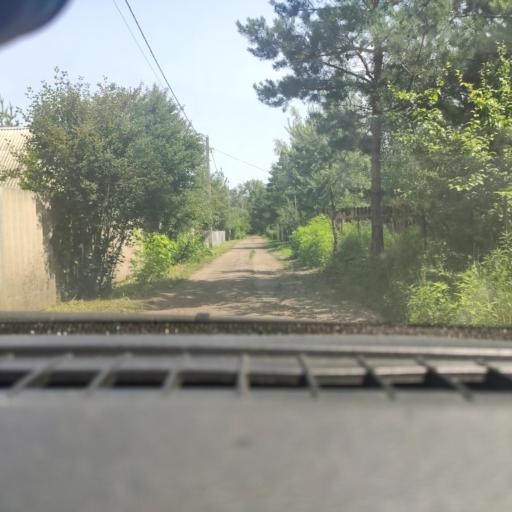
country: RU
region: Voronezj
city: Podgornoye
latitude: 51.8486
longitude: 39.2087
